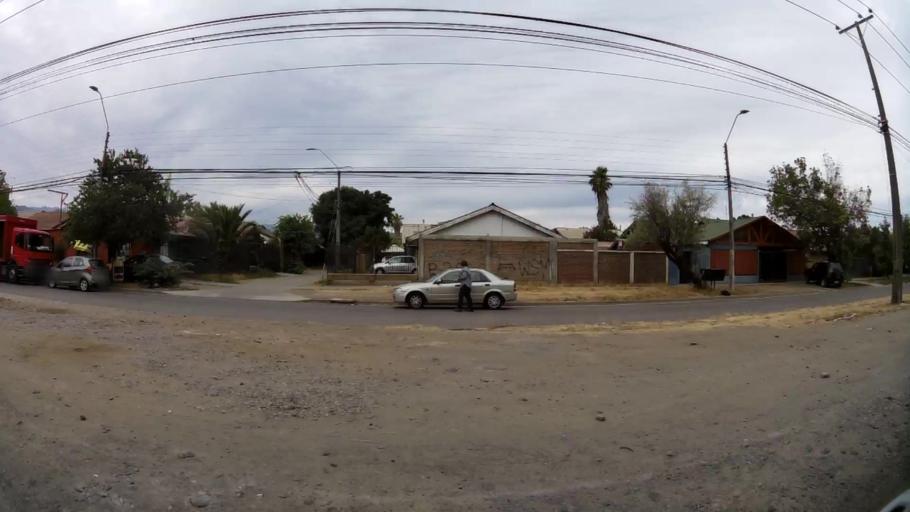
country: CL
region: O'Higgins
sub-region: Provincia de Cachapoal
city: Rancagua
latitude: -34.1416
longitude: -70.7373
